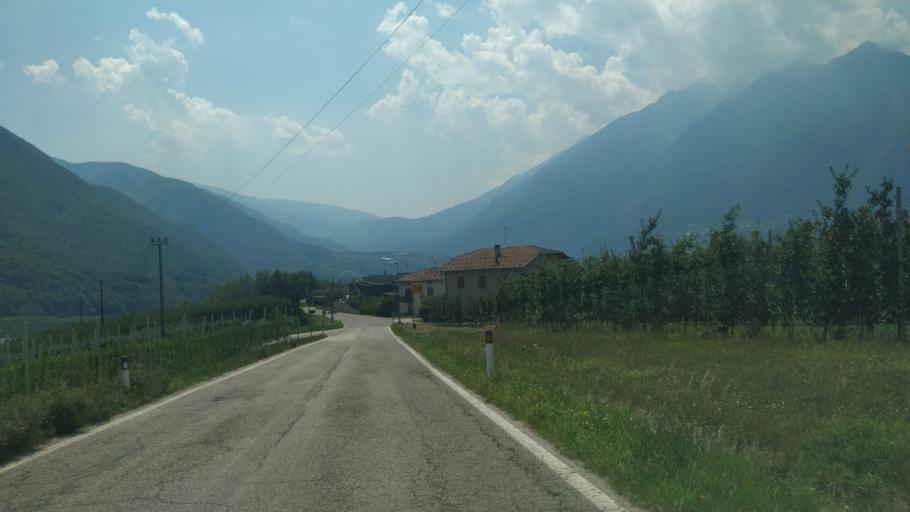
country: IT
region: Trentino-Alto Adige
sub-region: Provincia di Trento
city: Vigo di Ton
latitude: 46.2618
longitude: 11.0753
